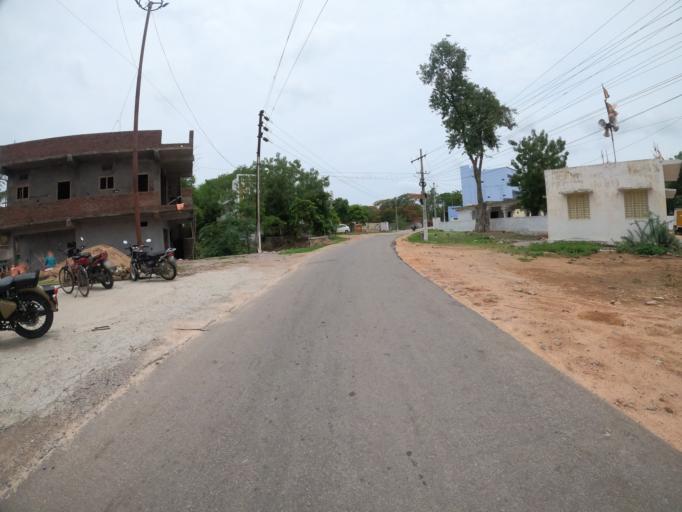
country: IN
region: Telangana
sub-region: Hyderabad
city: Hyderabad
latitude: 17.3387
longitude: 78.3632
